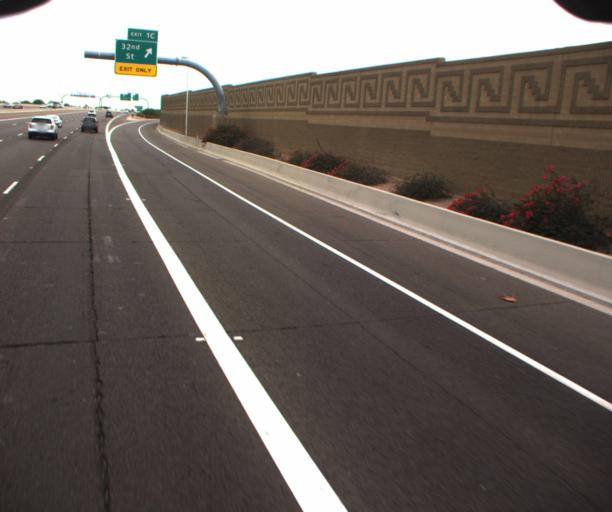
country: US
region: Arizona
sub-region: Maricopa County
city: Phoenix
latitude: 33.4617
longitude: -112.0183
